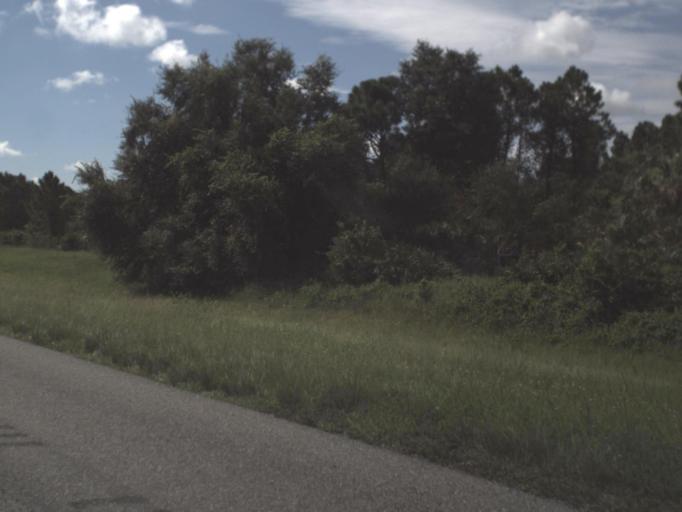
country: US
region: Florida
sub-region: Charlotte County
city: Port Charlotte
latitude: 27.0555
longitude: -82.0803
